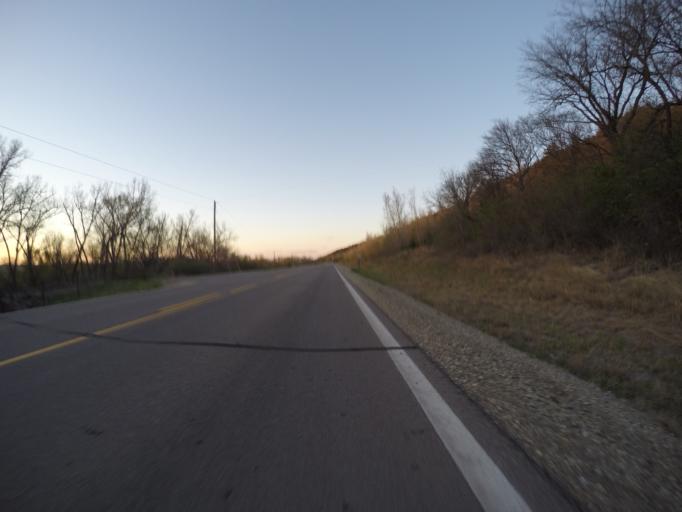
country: US
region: Kansas
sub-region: Riley County
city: Manhattan
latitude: 39.1409
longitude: -96.5588
